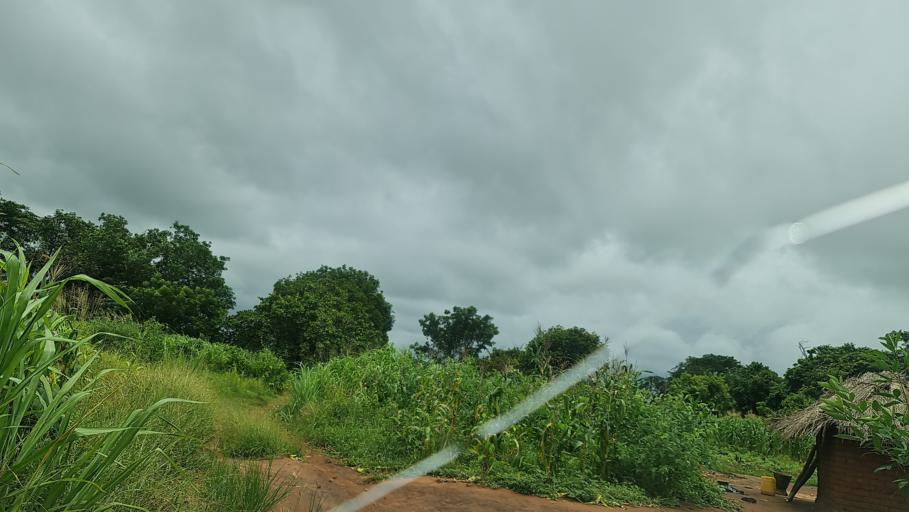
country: MW
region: Southern Region
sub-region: Nsanje District
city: Nsanje
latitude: -17.3890
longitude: 35.7812
